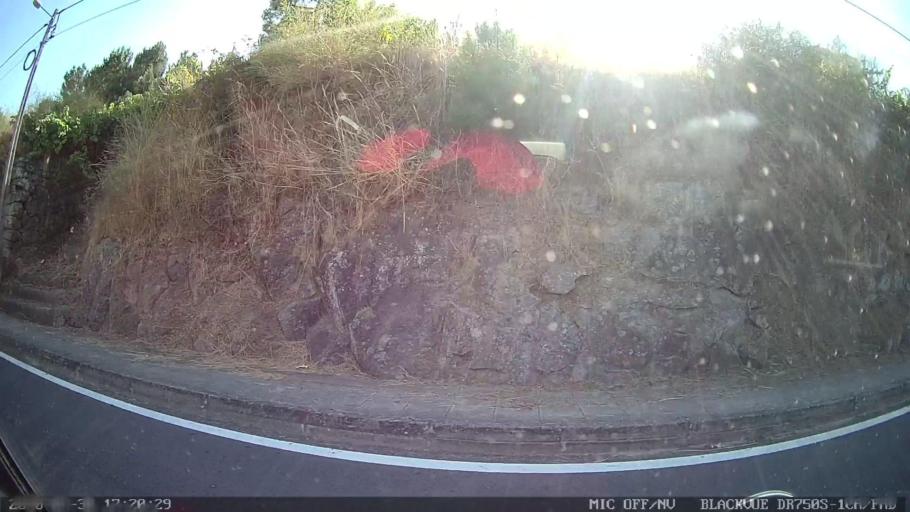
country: PT
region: Vila Real
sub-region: Sabrosa
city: Sabrosa
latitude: 41.2904
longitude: -7.4787
